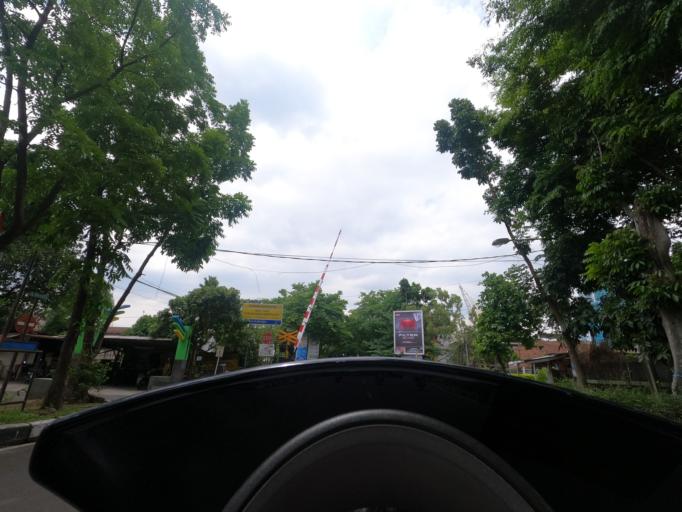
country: ID
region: West Java
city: Bandung
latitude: -6.9156
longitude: 107.6139
